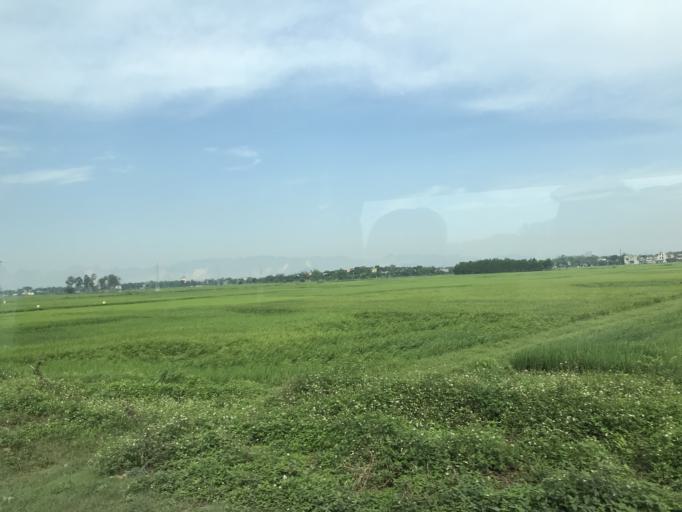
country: VN
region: Ha Nam
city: Thanh Pho Phu Ly
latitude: 20.5162
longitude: 105.9423
